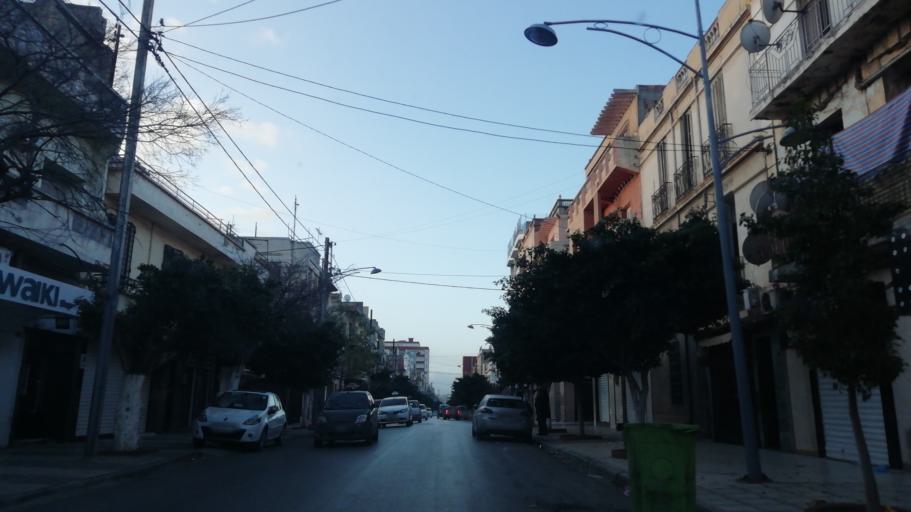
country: DZ
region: Oran
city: Oran
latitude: 35.6852
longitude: -0.6550
